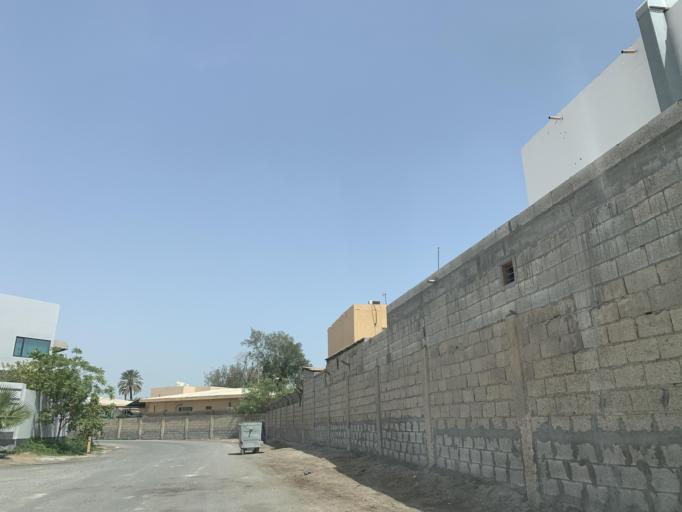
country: BH
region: Northern
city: Sitrah
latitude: 26.1577
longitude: 50.5920
